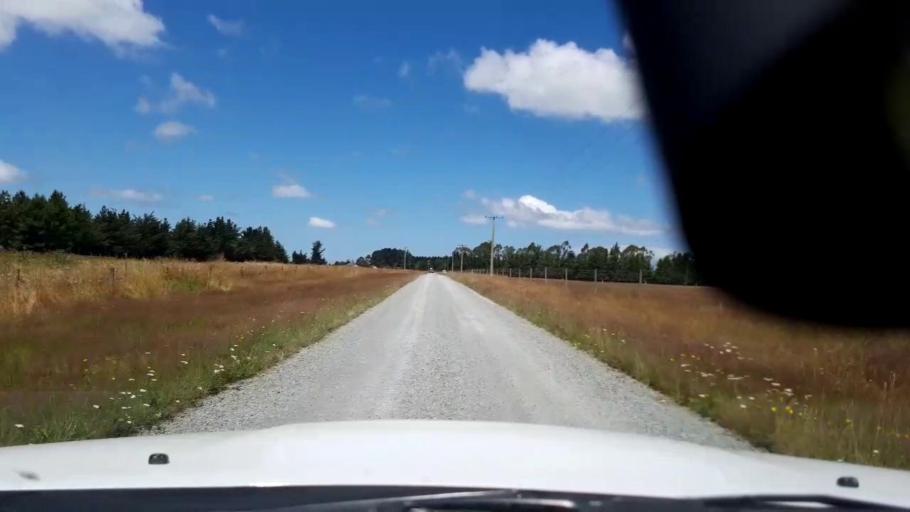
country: NZ
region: Canterbury
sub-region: Timaru District
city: Pleasant Point
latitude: -43.9885
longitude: 171.2906
